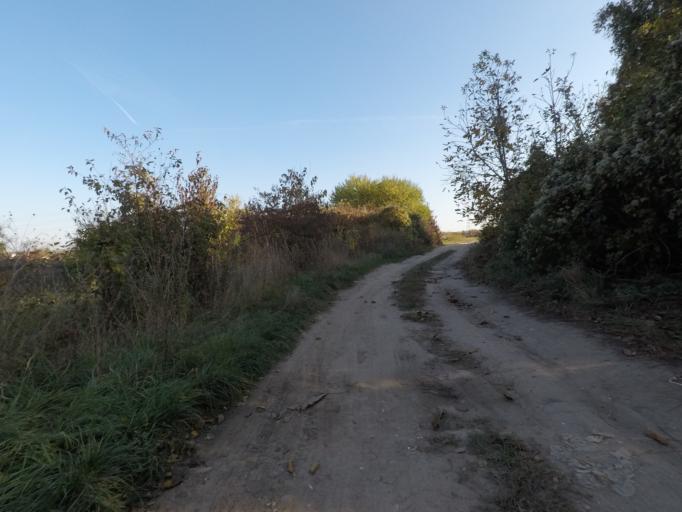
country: HU
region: Pest
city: Pomaz
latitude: 47.6327
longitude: 19.0334
